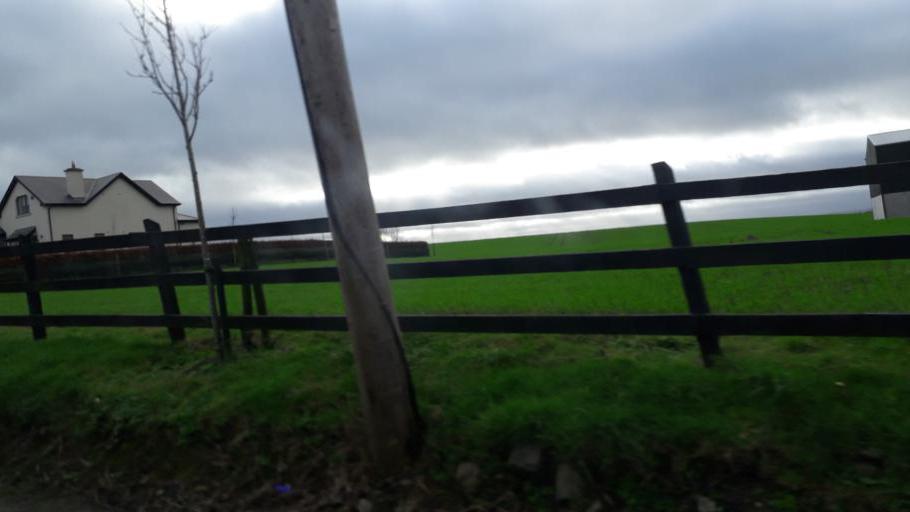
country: IE
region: Leinster
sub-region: Fingal County
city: Skerries
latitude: 53.5556
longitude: -6.1308
